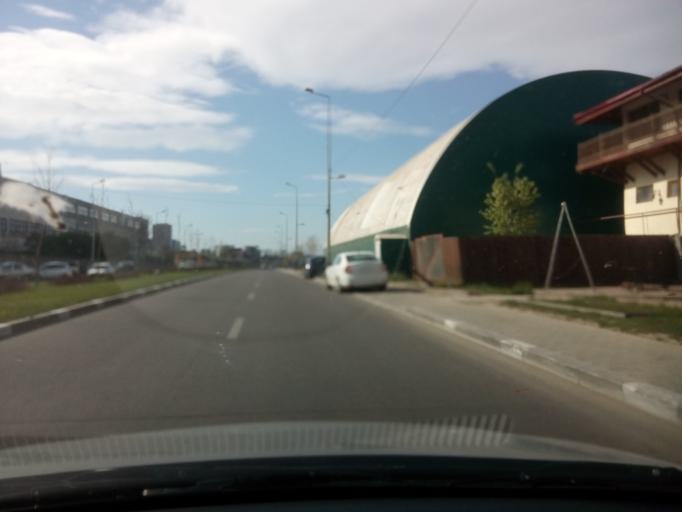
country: RO
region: Ilfov
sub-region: Comuna Fundeni-Dobroesti
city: Fundeni
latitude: 44.4458
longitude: 26.1569
